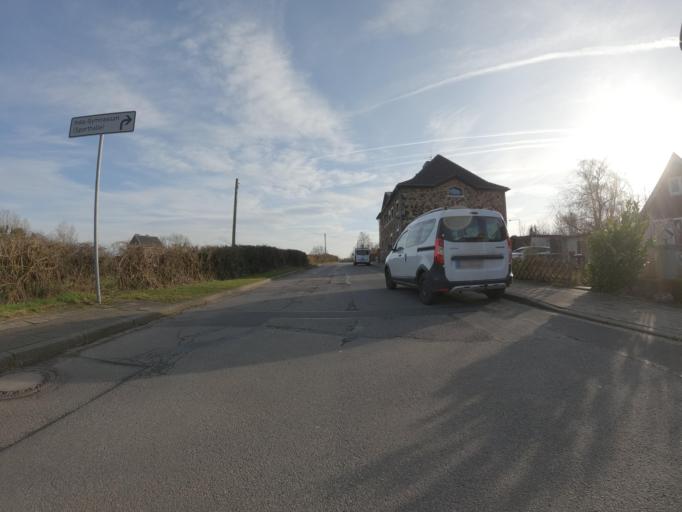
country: DE
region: North Rhine-Westphalia
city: Stolberg
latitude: 50.7266
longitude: 6.1800
